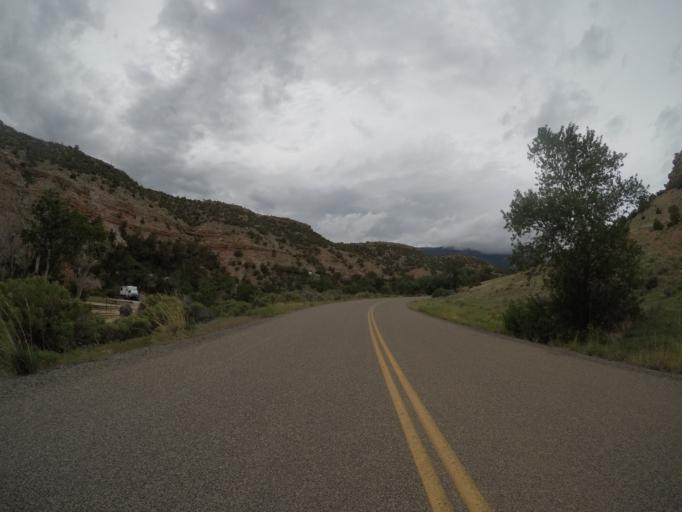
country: US
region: Wyoming
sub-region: Big Horn County
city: Lovell
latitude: 45.1029
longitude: -108.2229
